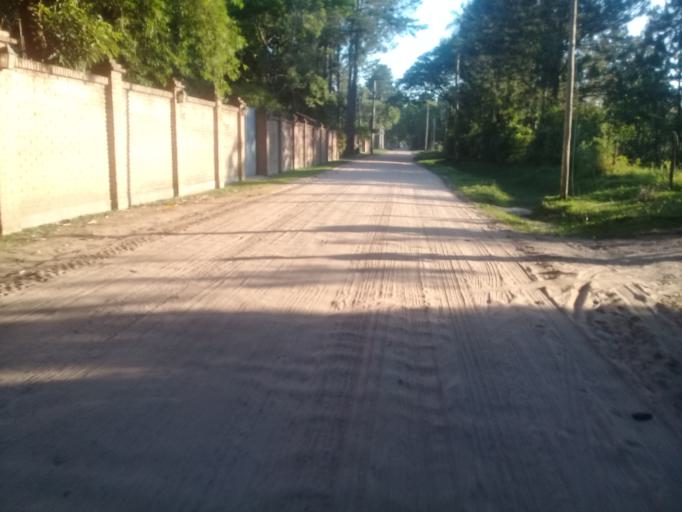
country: AR
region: Corrientes
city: San Luis del Palmar
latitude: -27.4620
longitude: -58.6614
